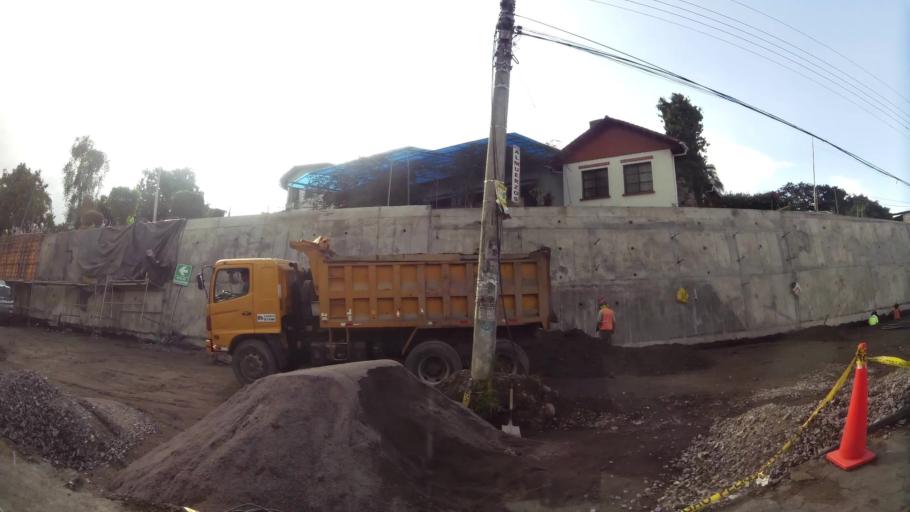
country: EC
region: Pichincha
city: Sangolqui
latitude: -0.3009
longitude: -78.4617
